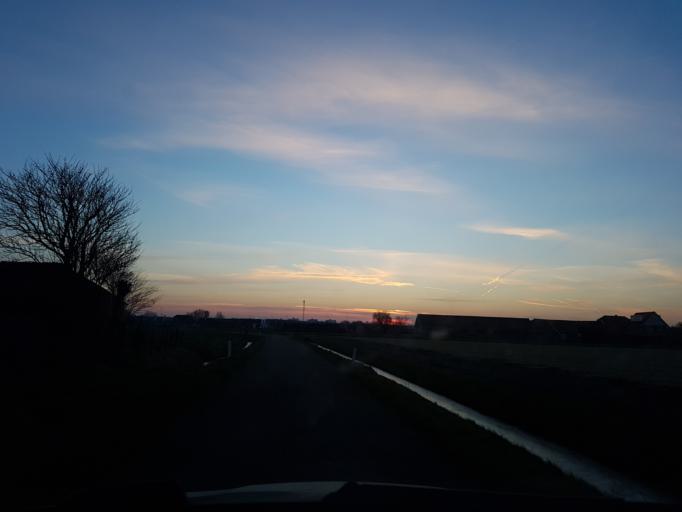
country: NL
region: South Holland
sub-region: Gemeente Noordwijk
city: Noordwijk-Binnen
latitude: 52.2187
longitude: 4.4420
